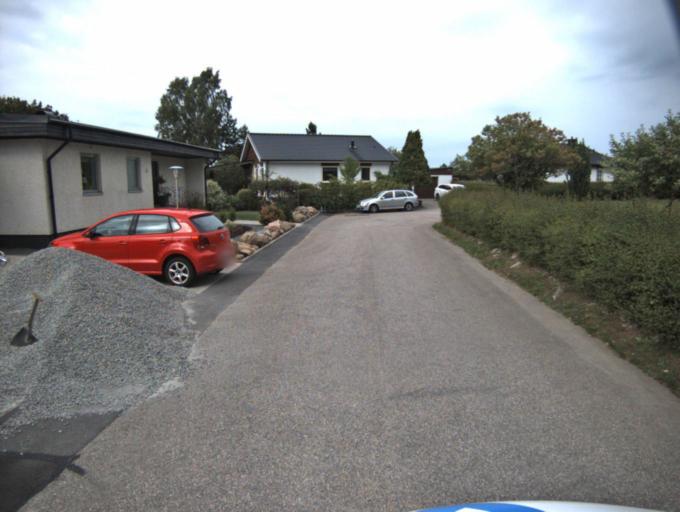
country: SE
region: Vaestra Goetaland
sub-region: Ulricehamns Kommun
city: Ulricehamn
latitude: 57.8387
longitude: 13.2880
